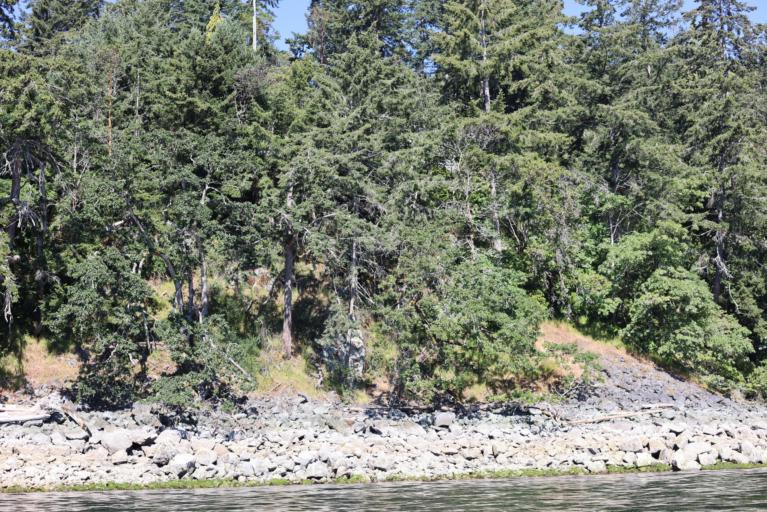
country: CA
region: British Columbia
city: North Cowichan
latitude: 48.8189
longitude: -123.6034
